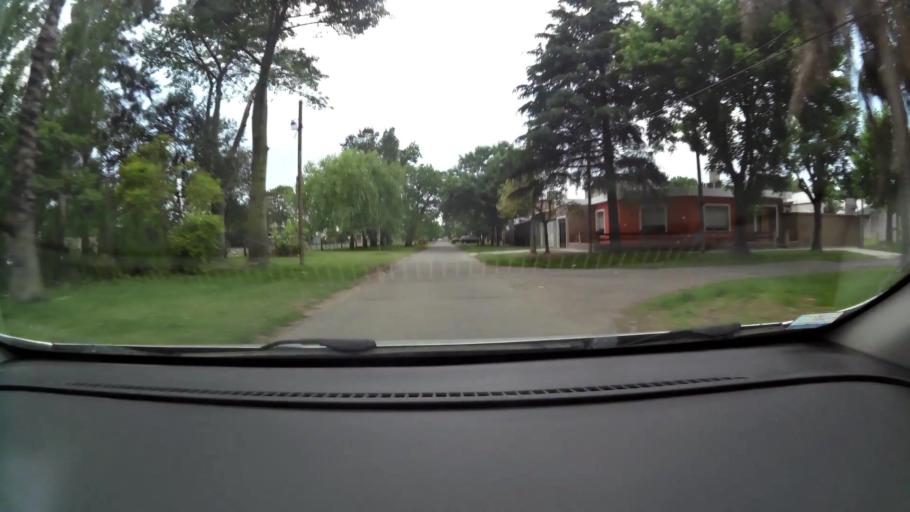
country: AR
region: Santa Fe
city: Granadero Baigorria
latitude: -32.8809
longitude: -60.7035
